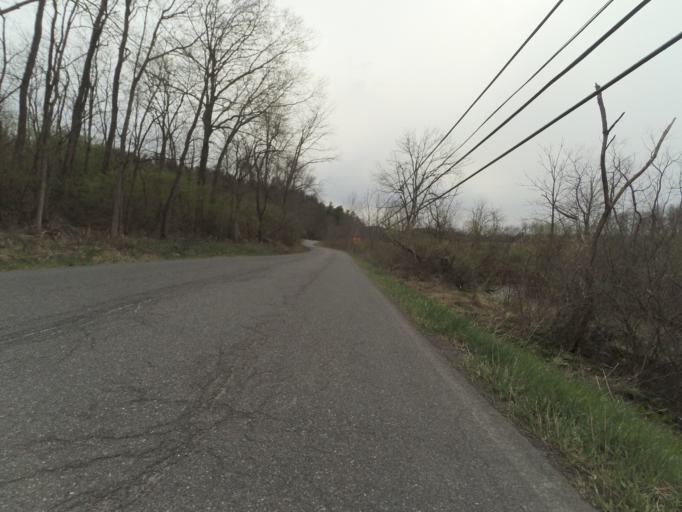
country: US
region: Pennsylvania
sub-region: Centre County
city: Milesburg
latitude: 40.9680
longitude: -77.7407
